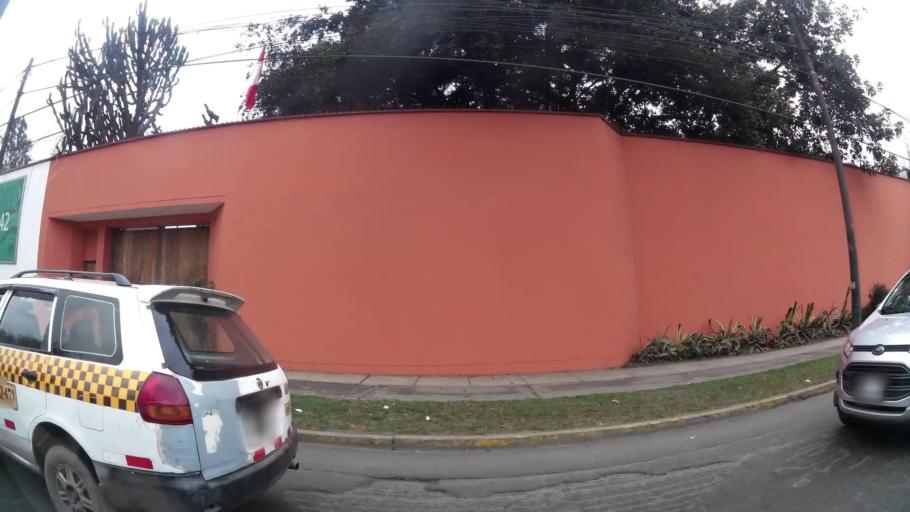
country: PE
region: Lima
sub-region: Lima
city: La Molina
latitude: -12.0801
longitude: -76.9662
